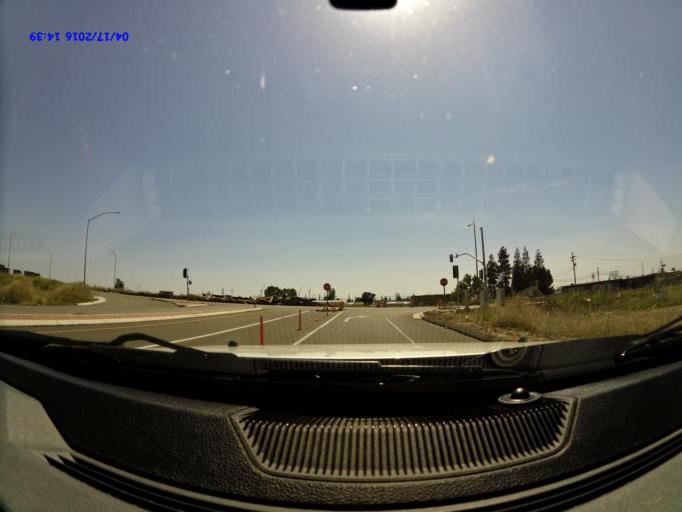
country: US
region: California
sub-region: San Joaquin County
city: Kennedy
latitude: 37.9354
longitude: -121.2359
